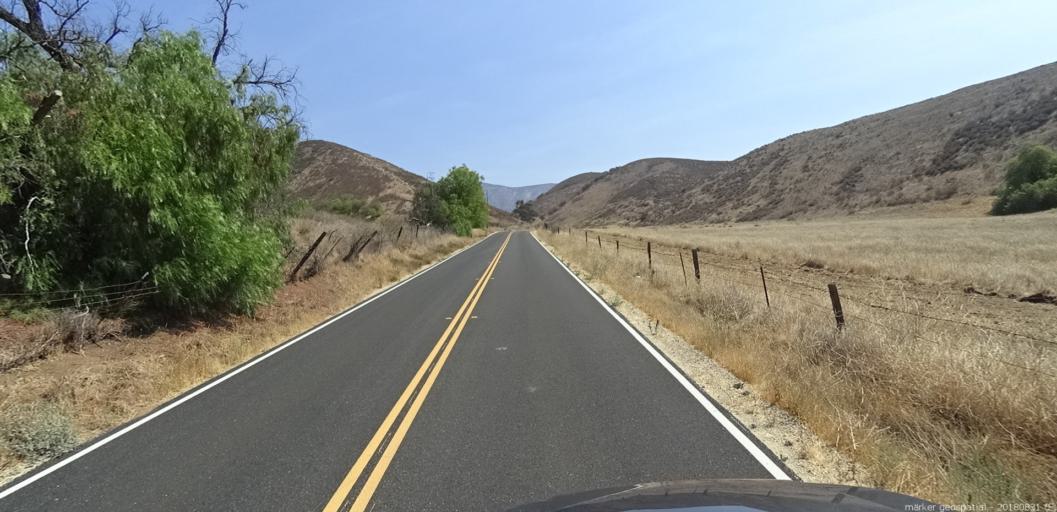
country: US
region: California
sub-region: Monterey County
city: Soledad
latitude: 36.4185
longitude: -121.2500
